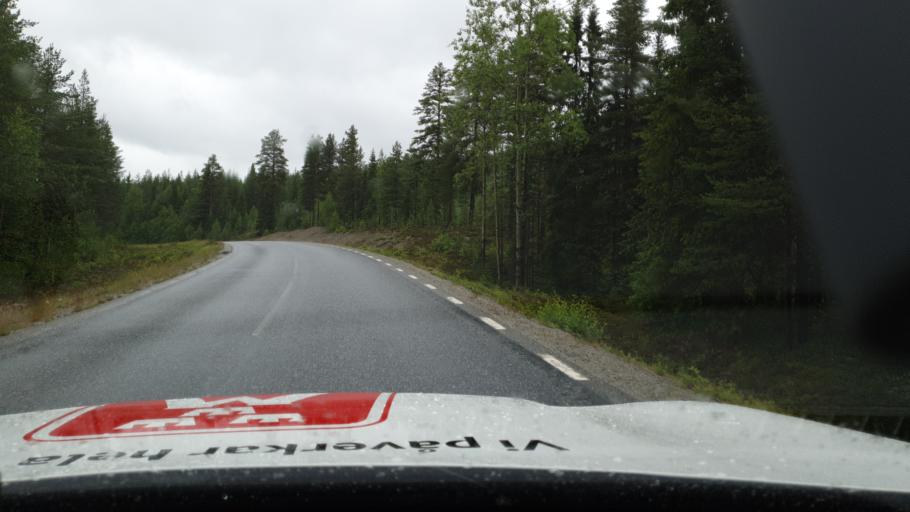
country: SE
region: Vaesterbotten
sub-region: Asele Kommun
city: Asele
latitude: 64.2041
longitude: 17.3345
